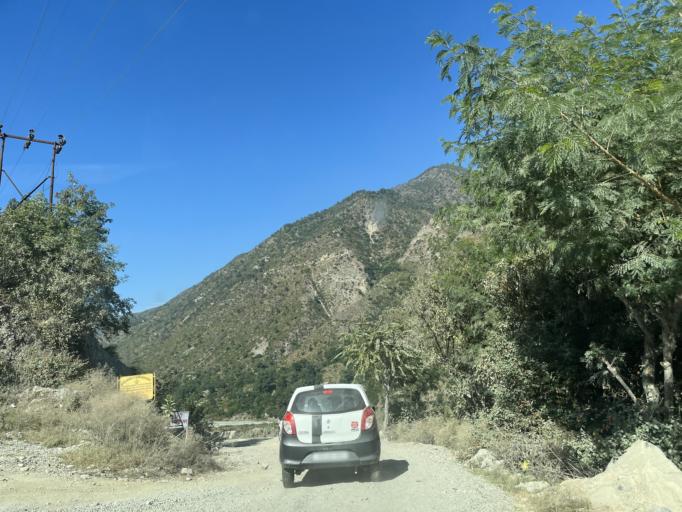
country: IN
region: Uttarakhand
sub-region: Almora
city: Ranikhet
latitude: 29.5534
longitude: 79.3967
